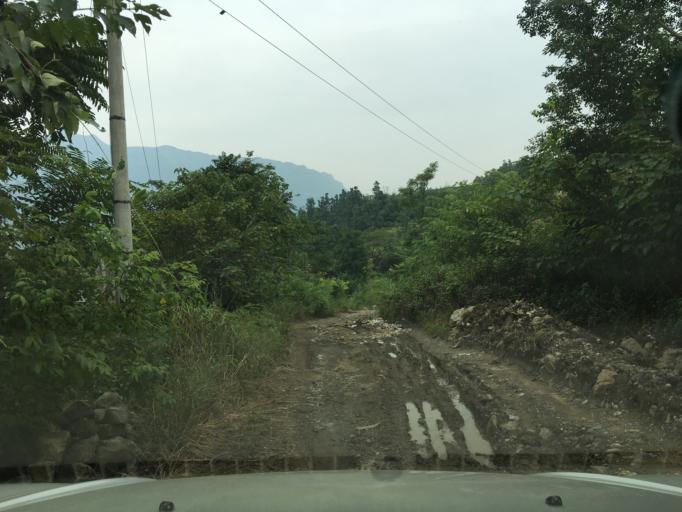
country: CN
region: Guizhou Sheng
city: Liupanshui
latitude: 26.0364
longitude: 105.1885
